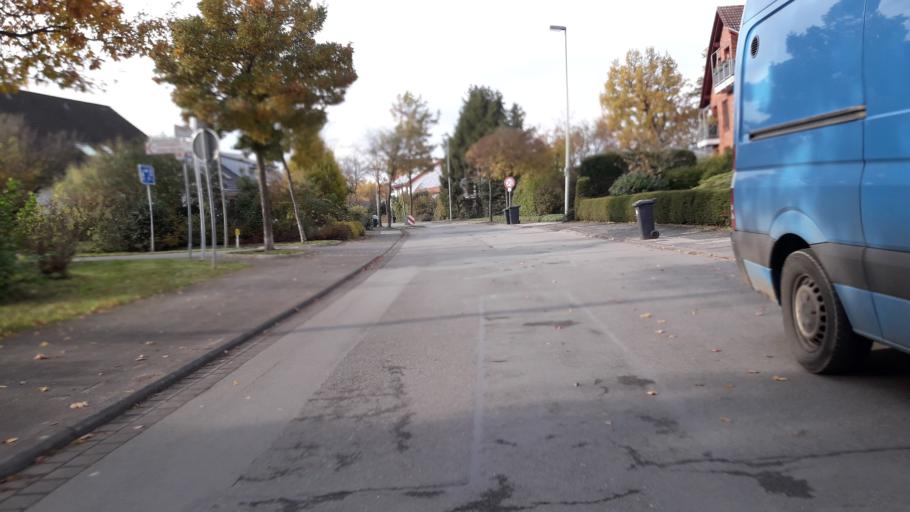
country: DE
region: North Rhine-Westphalia
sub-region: Regierungsbezirk Detmold
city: Schlangen
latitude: 51.7977
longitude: 8.8415
